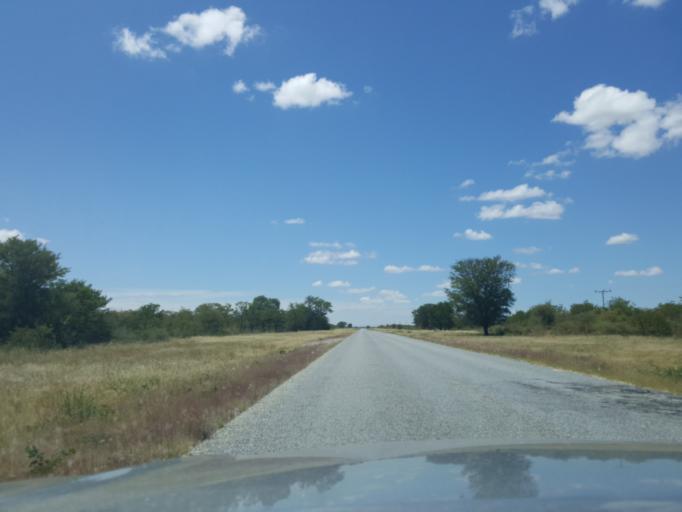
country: BW
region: Central
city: Gweta
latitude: -20.1351
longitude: 25.6541
